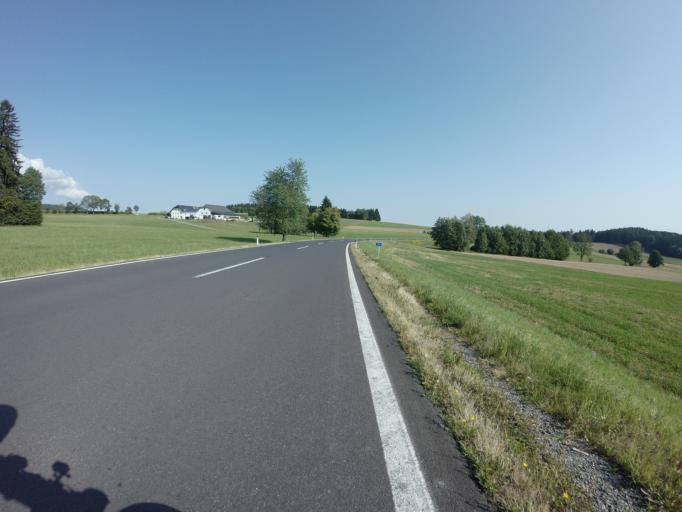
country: AT
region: Upper Austria
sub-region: Politischer Bezirk Urfahr-Umgebung
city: Bad Leonfelden
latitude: 48.5523
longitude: 14.3203
